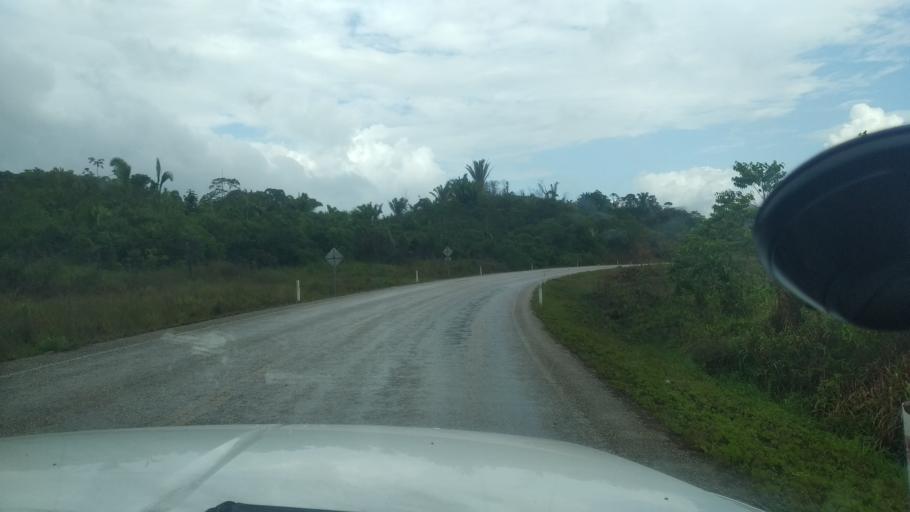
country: GT
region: Peten
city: San Luis
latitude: 16.1898
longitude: -89.1864
